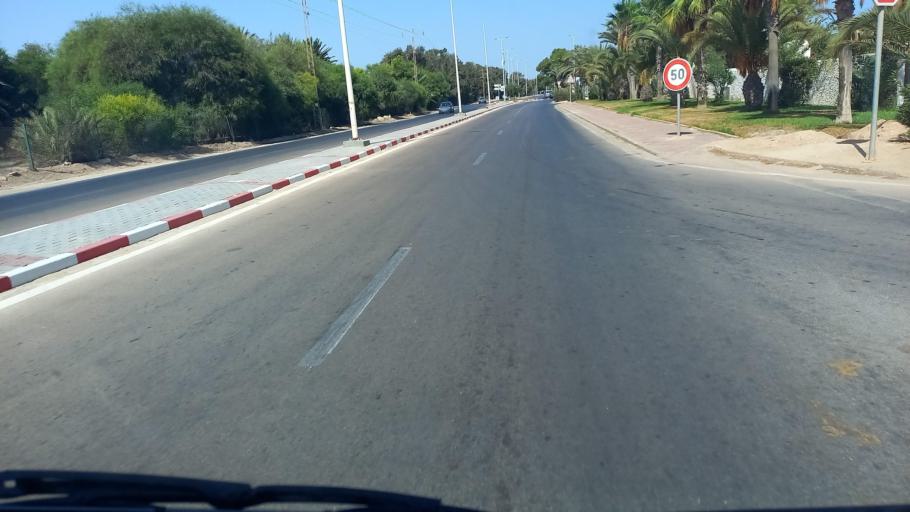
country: TN
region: Madanin
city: Midoun
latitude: 33.8260
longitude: 11.0176
